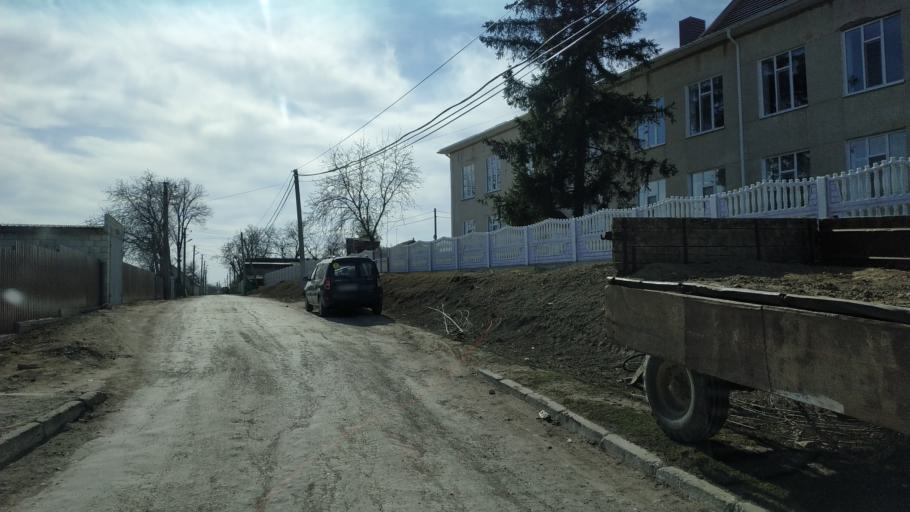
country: MD
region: Nisporeni
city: Nisporeni
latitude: 46.9629
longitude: 28.2107
